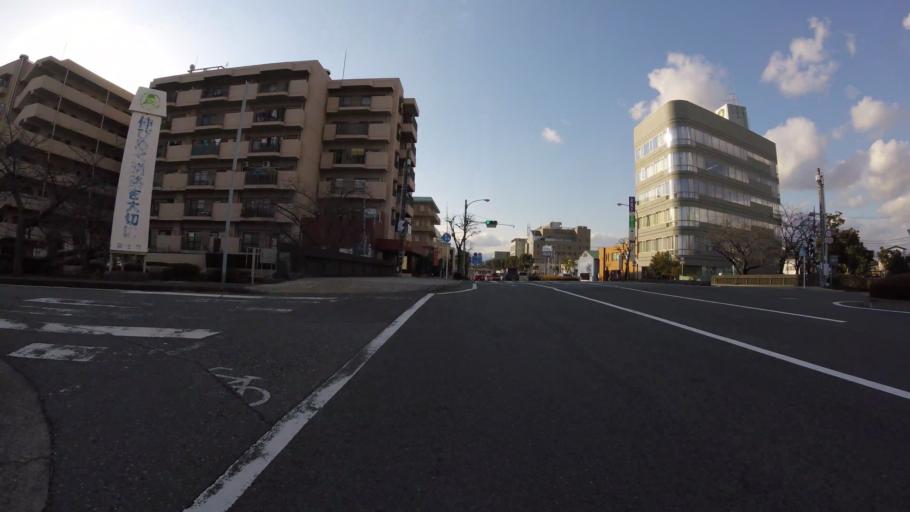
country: JP
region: Shizuoka
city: Fuji
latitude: 35.1602
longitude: 138.6800
